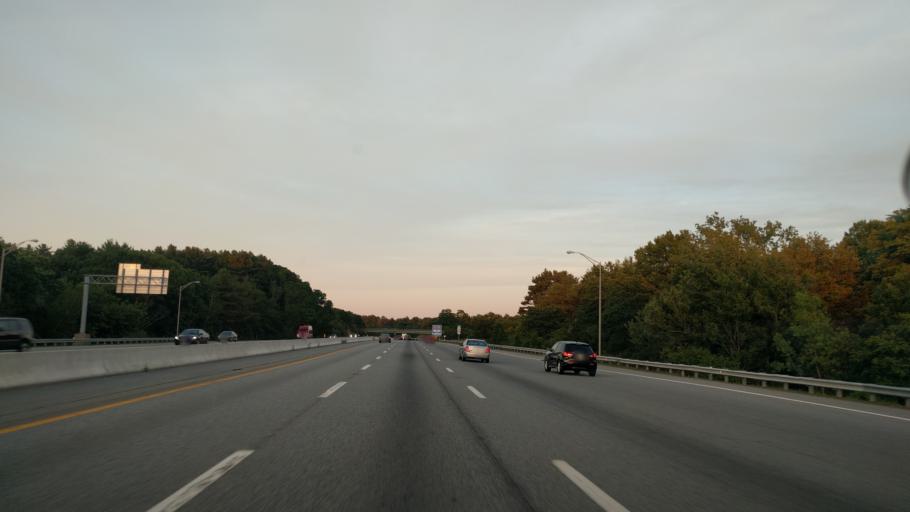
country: US
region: Massachusetts
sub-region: Middlesex County
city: Cochituate
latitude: 42.3120
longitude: -71.3802
